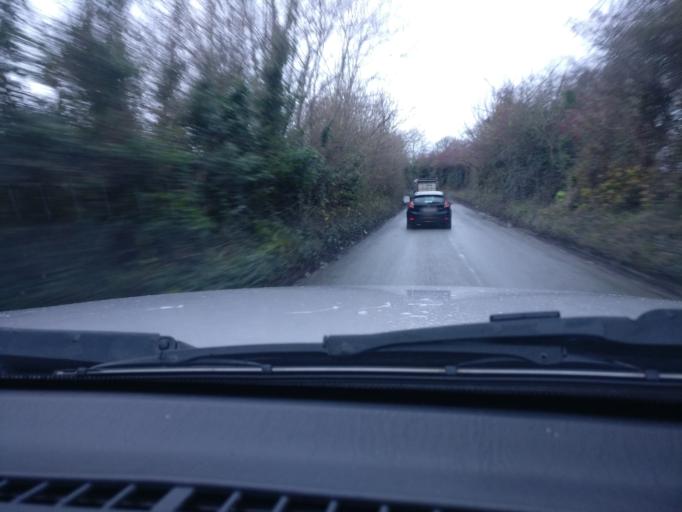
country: IE
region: Leinster
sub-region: An Mhi
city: Longwood
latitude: 53.4429
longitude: -6.9799
